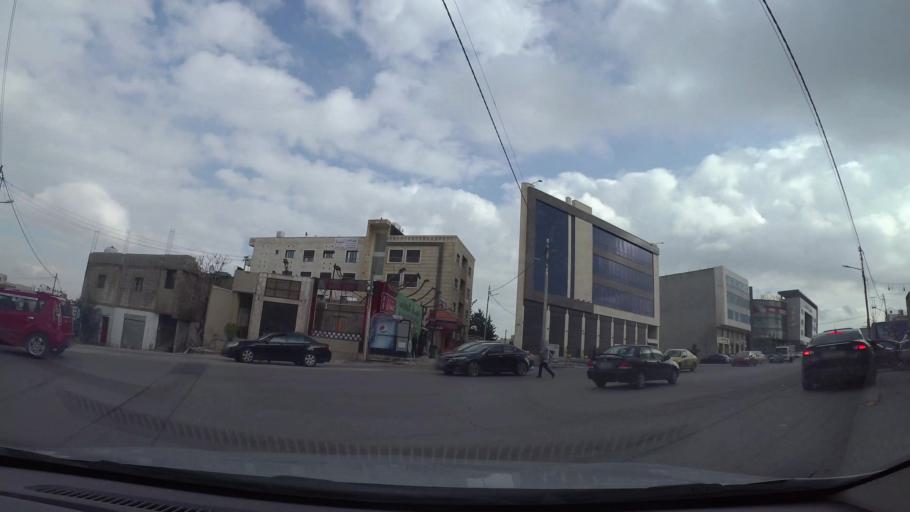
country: JO
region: Amman
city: Al Jubayhah
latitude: 31.9880
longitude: 35.8485
